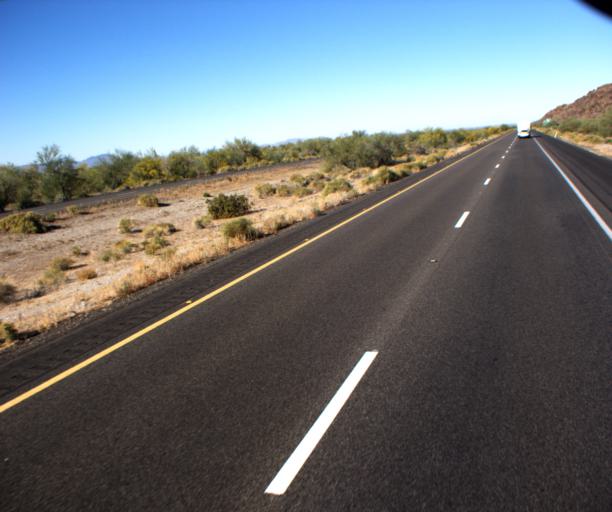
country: US
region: Arizona
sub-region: Maricopa County
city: Gila Bend
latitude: 32.9068
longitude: -112.5589
